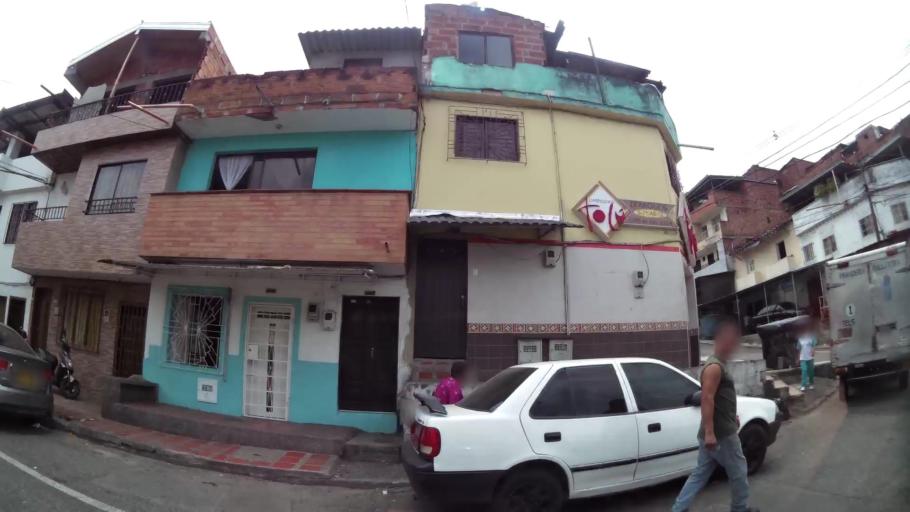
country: CO
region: Antioquia
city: Medellin
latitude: 6.2747
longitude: -75.5496
